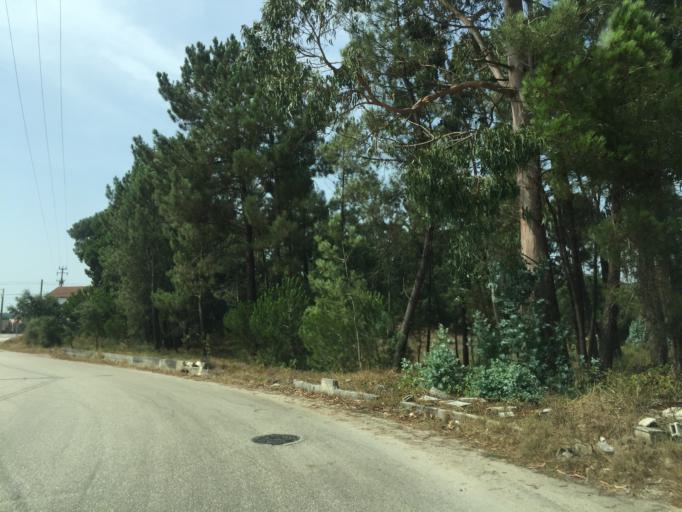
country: PT
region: Leiria
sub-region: Leiria
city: Amor
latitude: 39.7956
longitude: -8.8339
